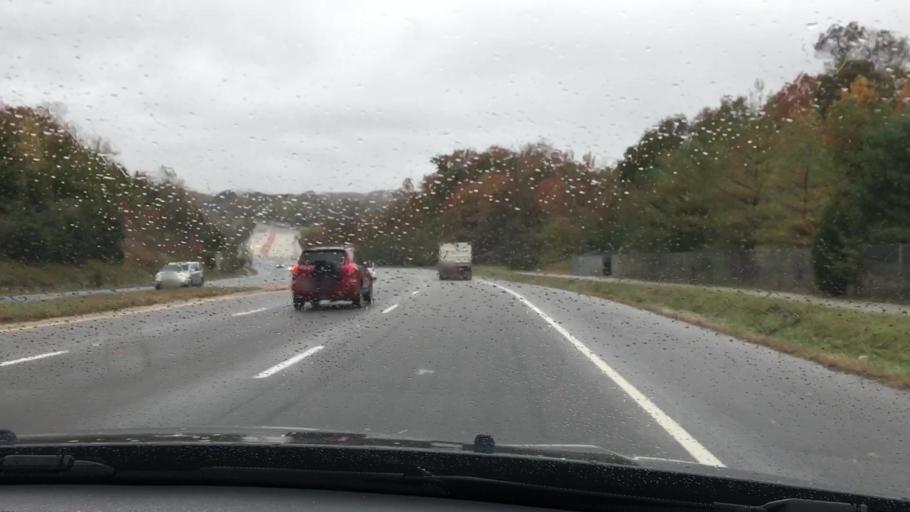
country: US
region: Virginia
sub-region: Prince William County
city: Woodbridge
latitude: 38.6890
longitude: -77.2575
